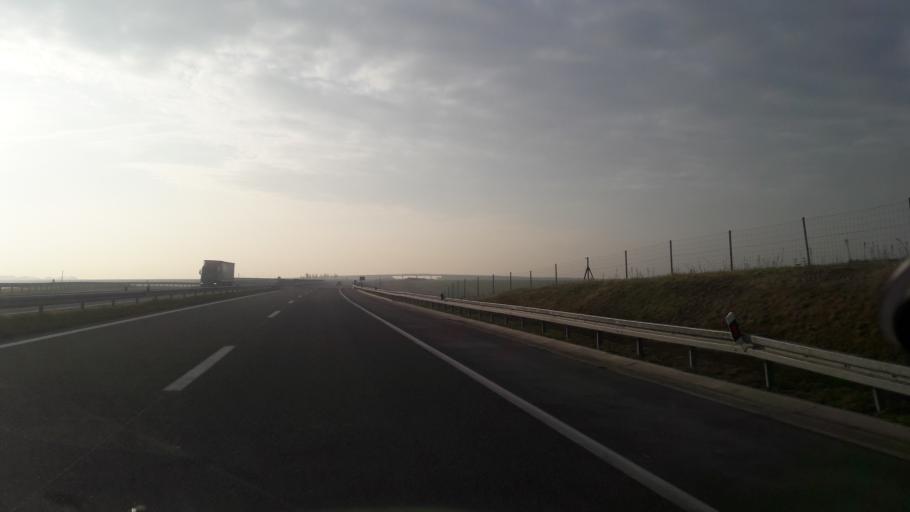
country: HR
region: Osjecko-Baranjska
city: Gorjani
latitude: 45.3593
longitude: 18.3994
